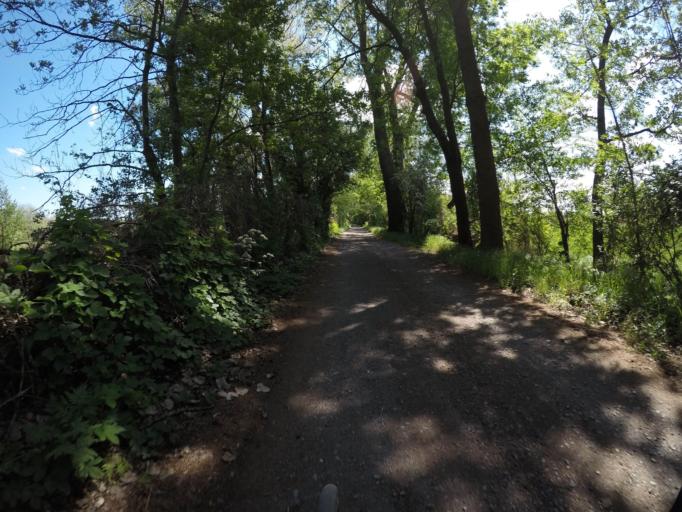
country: DE
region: Brandenburg
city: Werder
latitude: 52.4111
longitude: 12.9448
